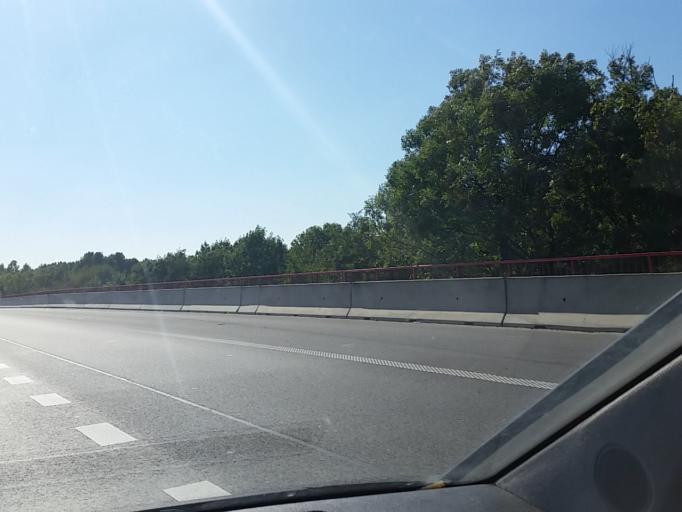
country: BE
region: Flanders
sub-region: Provincie Vlaams-Brabant
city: Dilbeek
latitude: 50.8689
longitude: 4.2697
